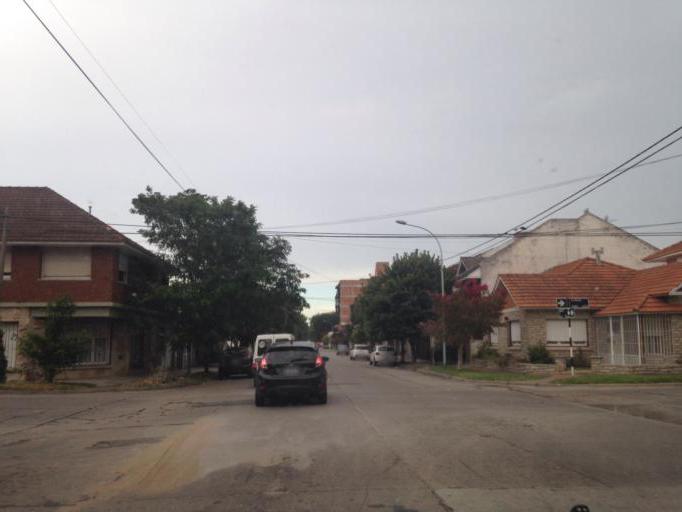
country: AR
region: Buenos Aires
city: Mar del Plata
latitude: -38.0181
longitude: -57.5679
